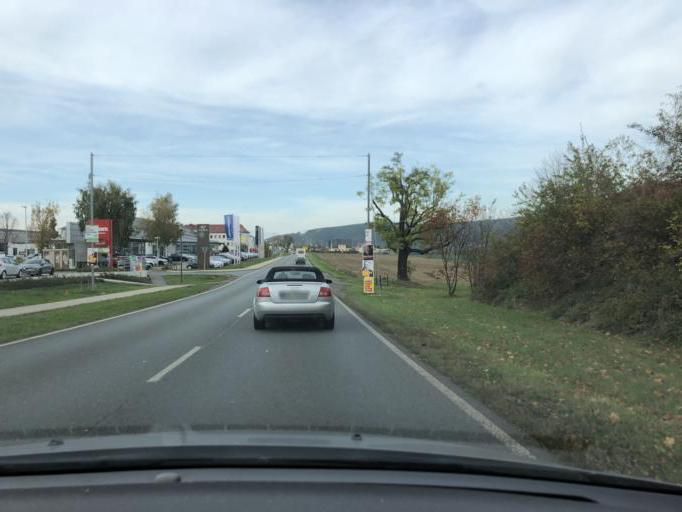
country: DE
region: Thuringia
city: Saalfeld
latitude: 50.6542
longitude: 11.3506
